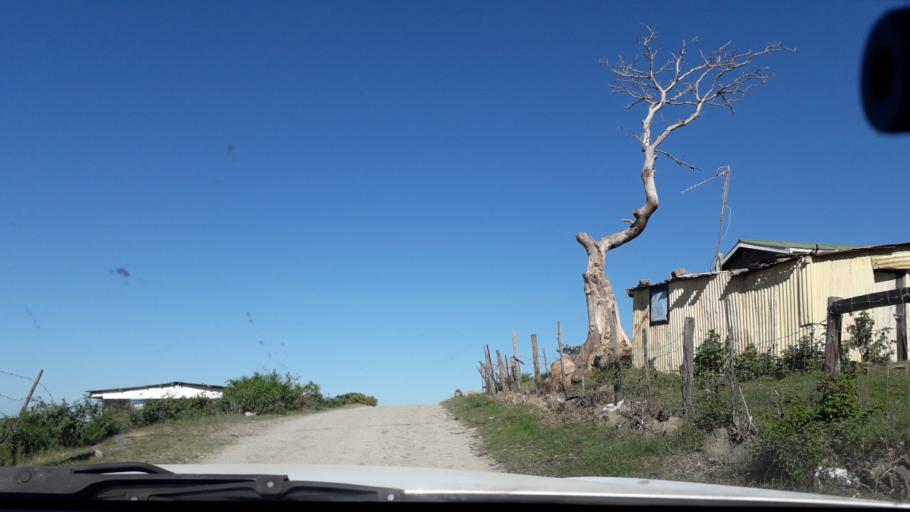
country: ZA
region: Eastern Cape
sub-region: Buffalo City Metropolitan Municipality
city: East London
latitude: -32.8438
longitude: 27.9894
